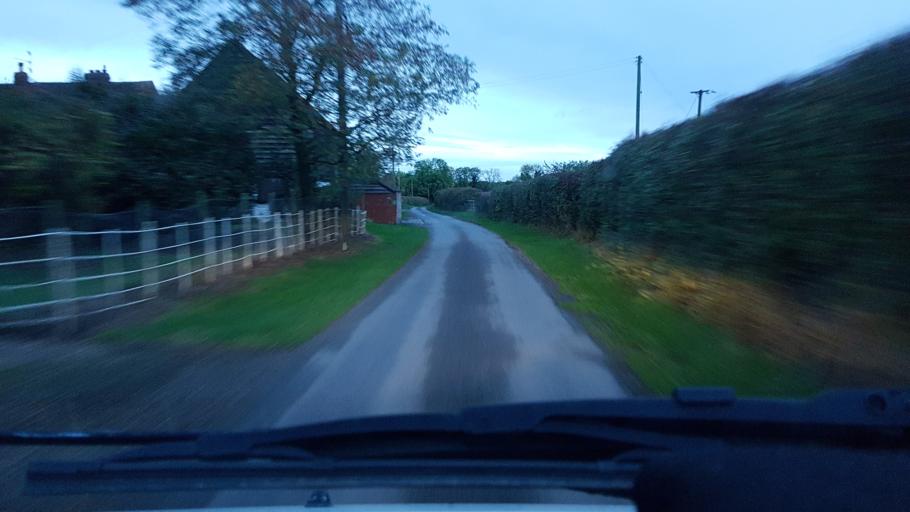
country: GB
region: England
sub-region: Worcestershire
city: Upton upon Severn
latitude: 52.0564
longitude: -2.2755
